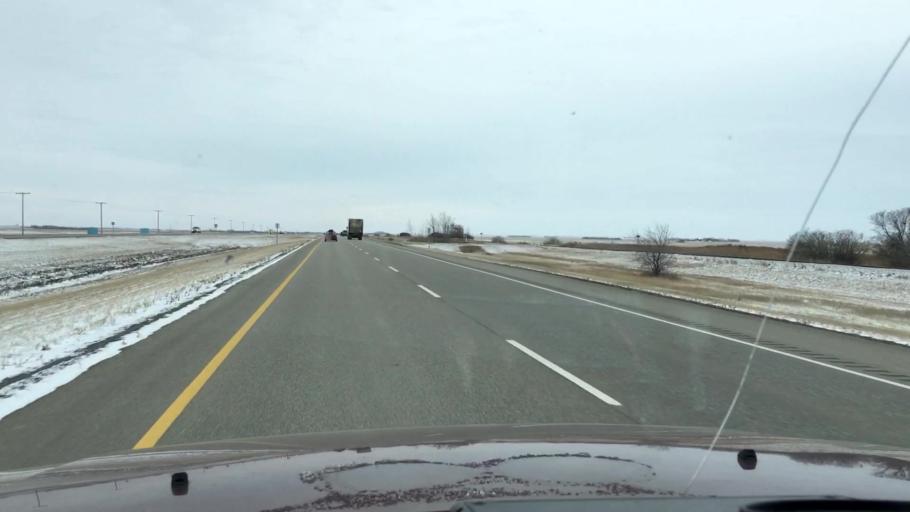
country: CA
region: Saskatchewan
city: Watrous
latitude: 51.1924
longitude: -105.9501
